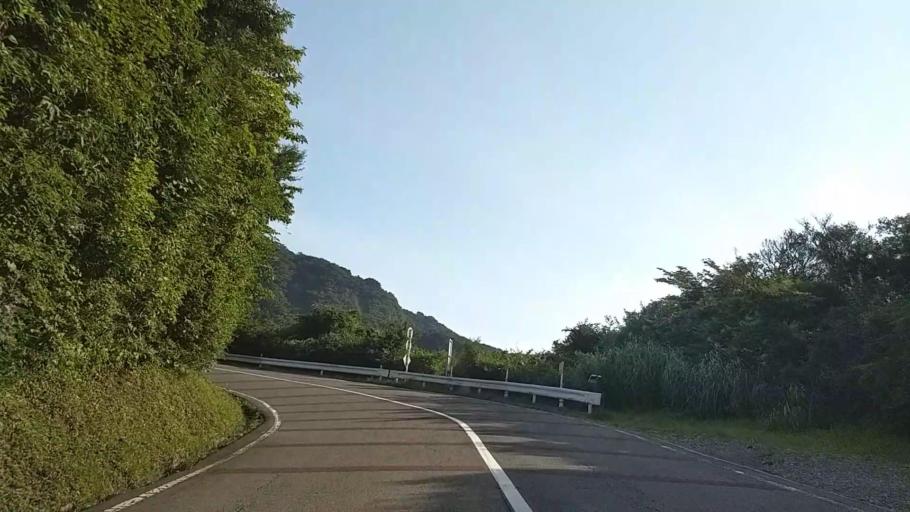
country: JP
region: Kanagawa
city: Hakone
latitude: 35.2241
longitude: 138.9818
